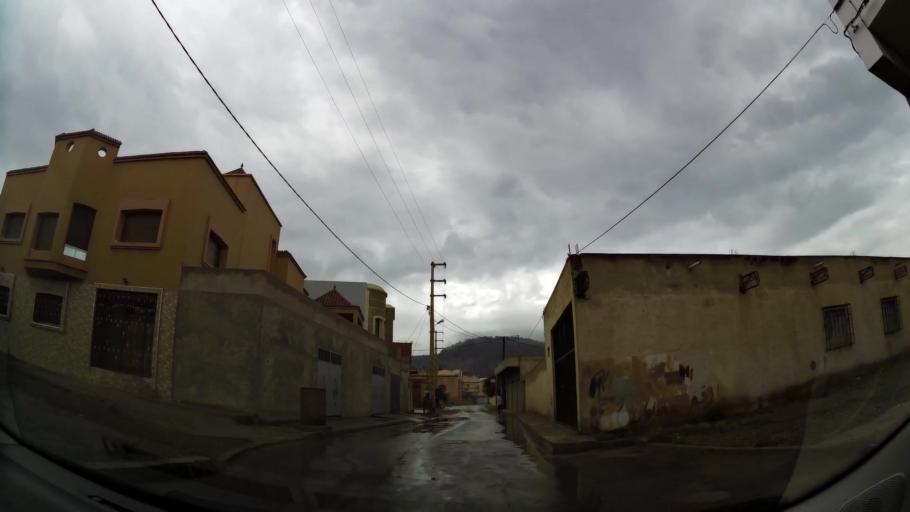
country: MA
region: Oriental
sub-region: Nador
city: Nador
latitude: 35.1504
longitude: -2.9953
